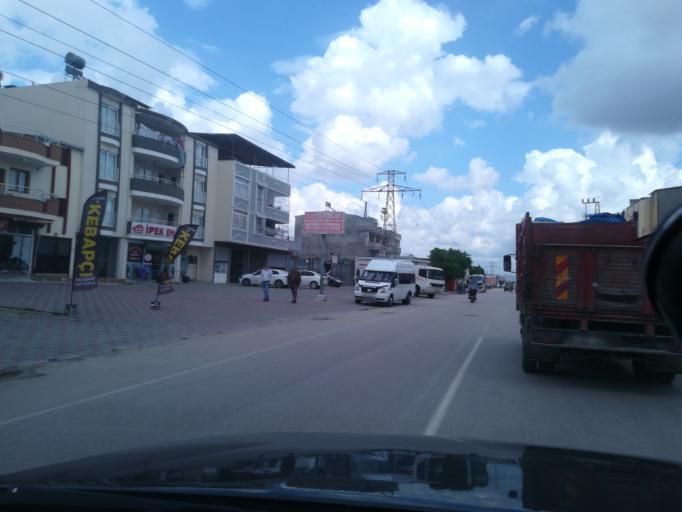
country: TR
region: Adana
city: Yuregir
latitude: 36.9770
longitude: 35.3849
